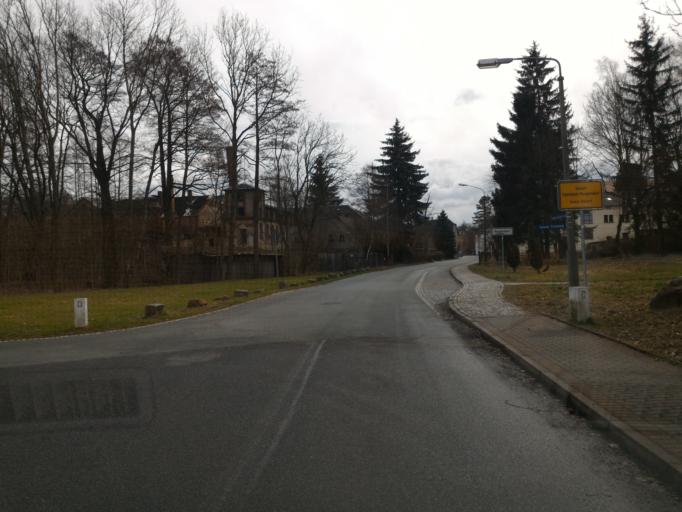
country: DE
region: Saxony
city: Neugersdorf
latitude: 50.9835
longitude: 14.5987
